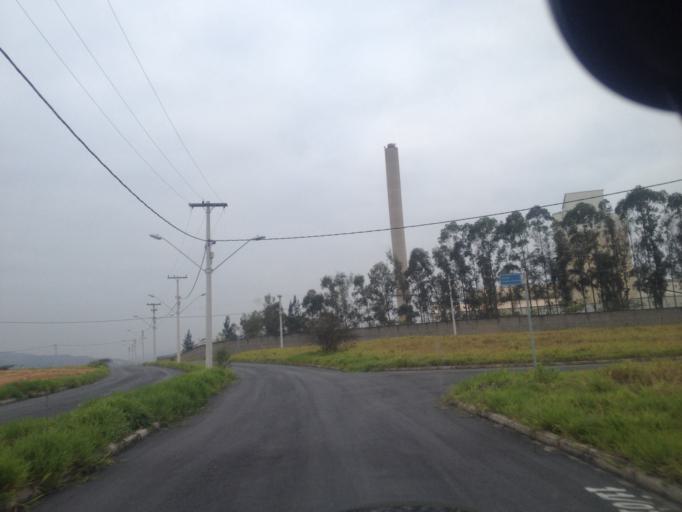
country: BR
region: Rio de Janeiro
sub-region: Porto Real
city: Porto Real
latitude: -22.4204
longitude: -44.3121
